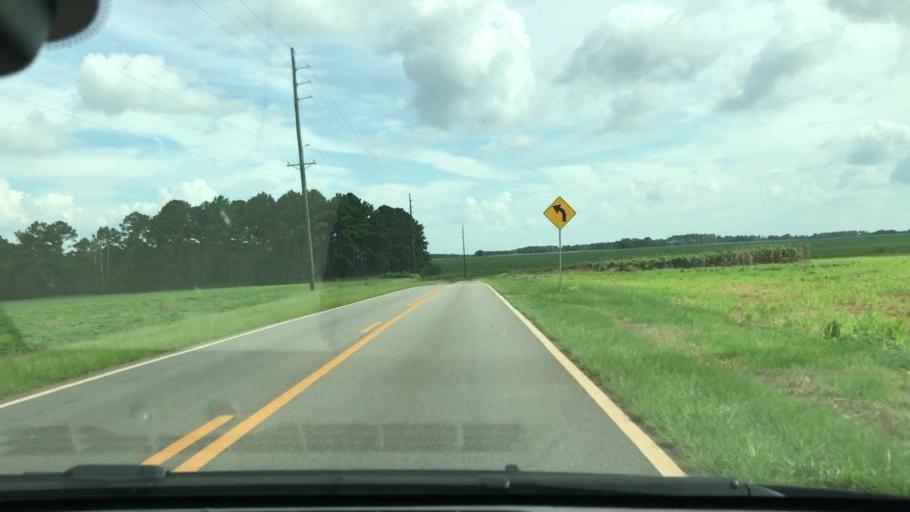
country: US
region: Georgia
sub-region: Clay County
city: Fort Gaines
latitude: 31.5351
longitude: -84.9592
